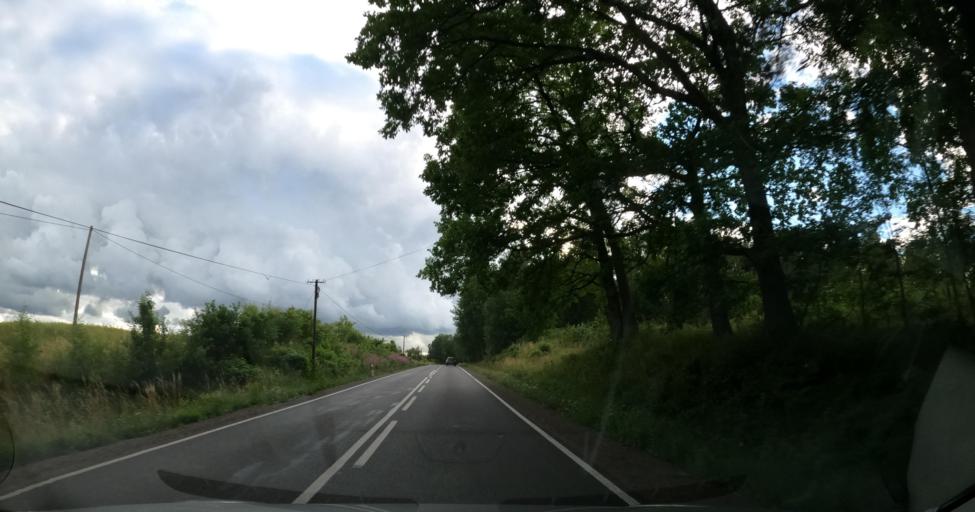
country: PL
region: Pomeranian Voivodeship
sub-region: Powiat bytowski
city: Czarna Dabrowka
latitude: 54.3456
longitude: 17.5902
